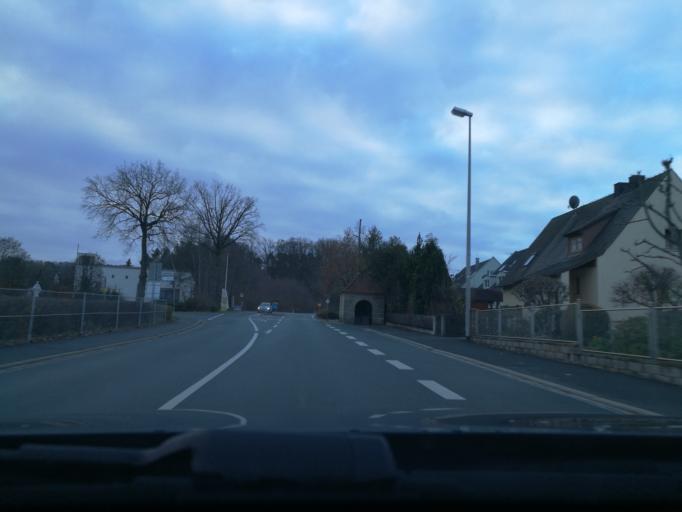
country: DE
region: Bavaria
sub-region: Upper Franconia
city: Langensendelbach
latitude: 49.6385
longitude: 11.0695
